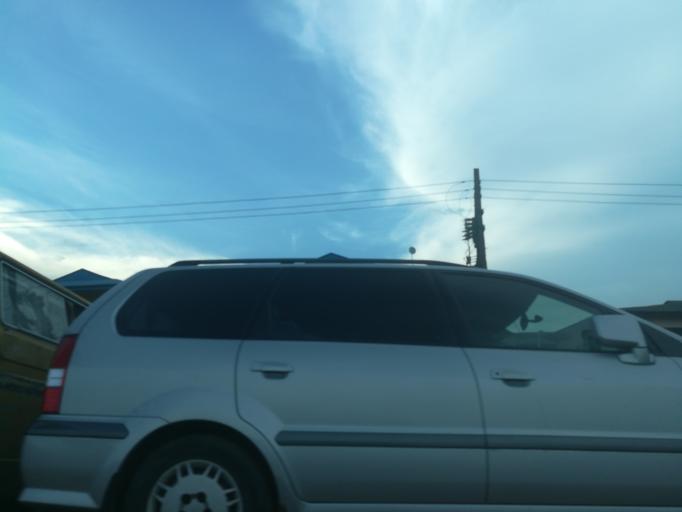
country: NG
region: Lagos
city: Ebute Ikorodu
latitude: 6.6213
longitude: 3.4808
